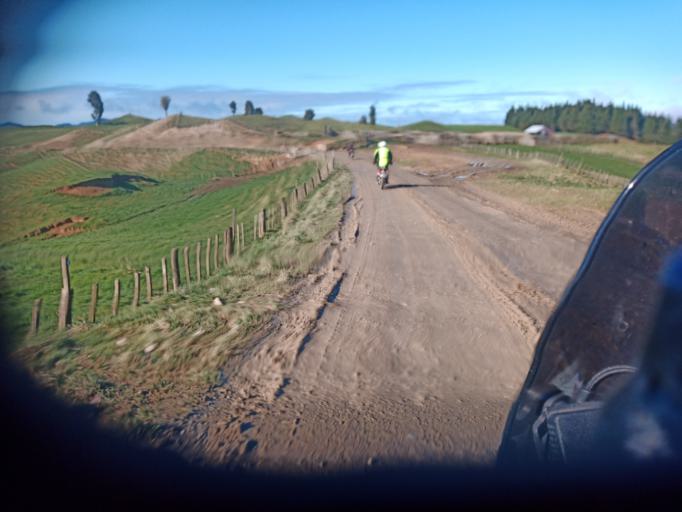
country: NZ
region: Gisborne
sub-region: Gisborne District
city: Gisborne
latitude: -38.1858
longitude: 178.0874
